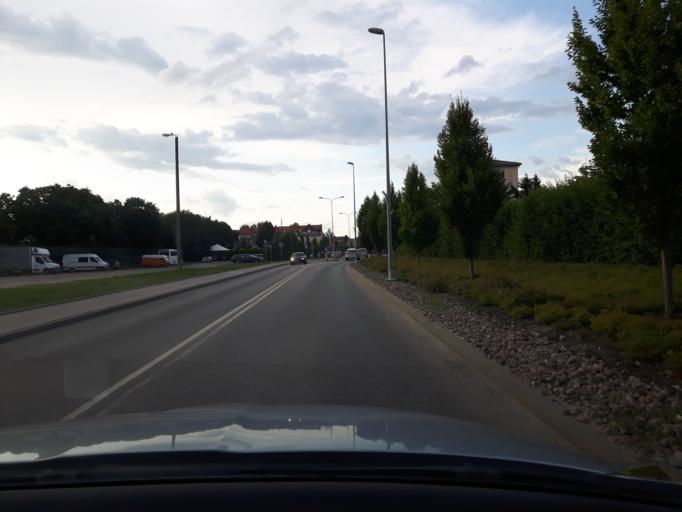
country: PL
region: Pomeranian Voivodeship
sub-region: Sopot
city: Sopot
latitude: 54.4284
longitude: 18.5749
